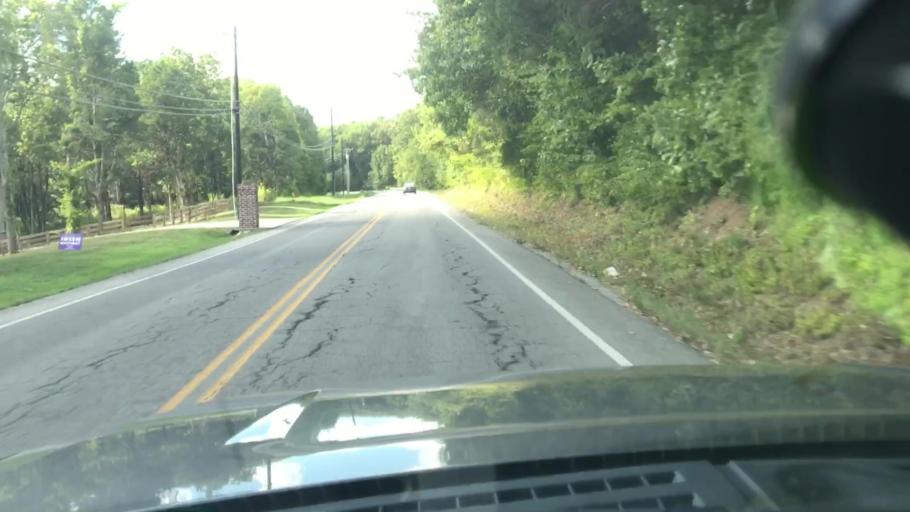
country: US
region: Tennessee
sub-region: Davidson County
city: Forest Hills
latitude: 36.0232
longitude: -86.8899
